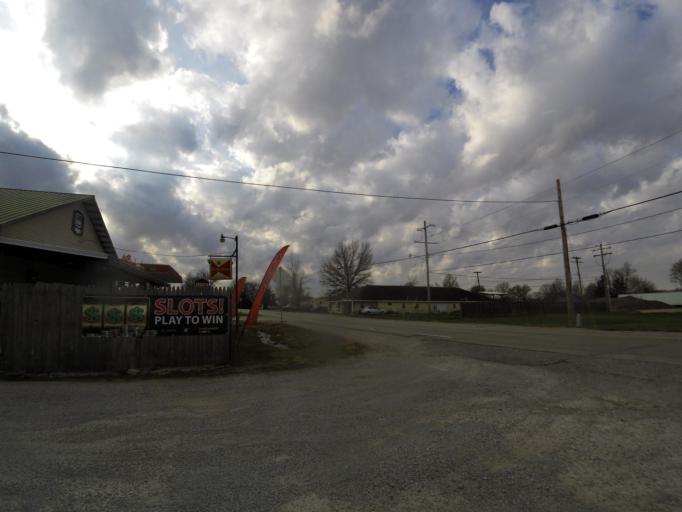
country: US
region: Illinois
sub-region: Fayette County
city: Ramsey
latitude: 39.1399
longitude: -89.1082
